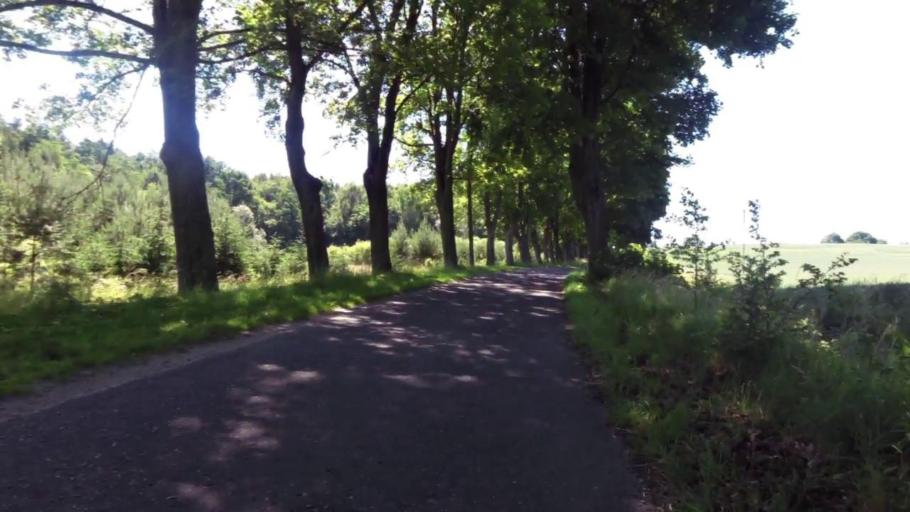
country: PL
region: West Pomeranian Voivodeship
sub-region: Powiat swidwinski
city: Rabino
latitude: 53.8556
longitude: 15.9776
